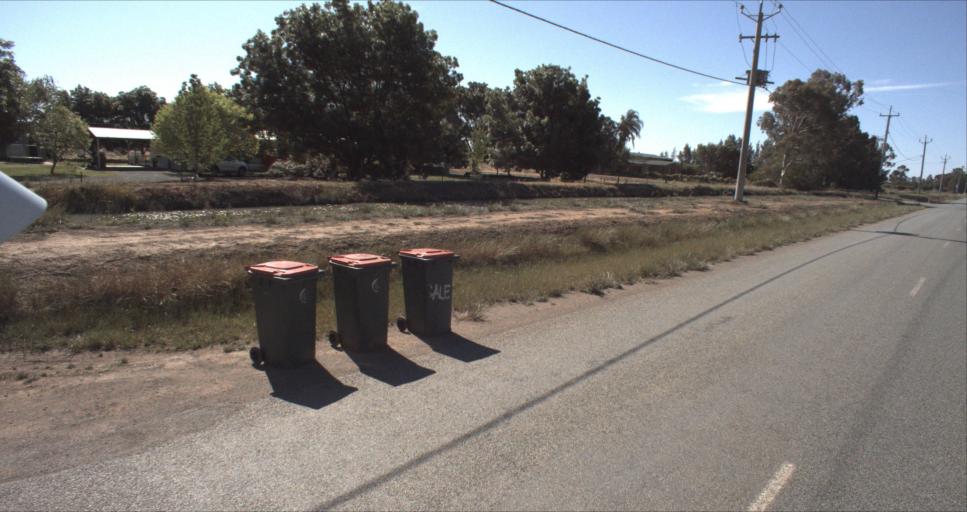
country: AU
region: New South Wales
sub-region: Leeton
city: Leeton
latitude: -34.5637
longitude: 146.3831
